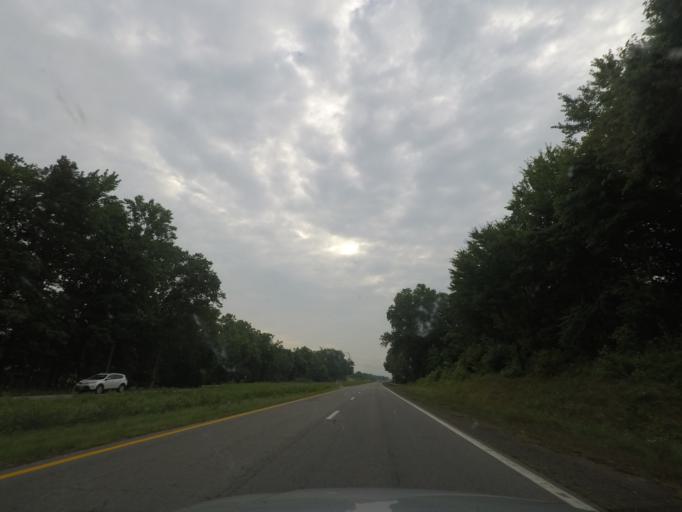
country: US
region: Virginia
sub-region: Mecklenburg County
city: Chase City
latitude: 36.8608
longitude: -78.5949
